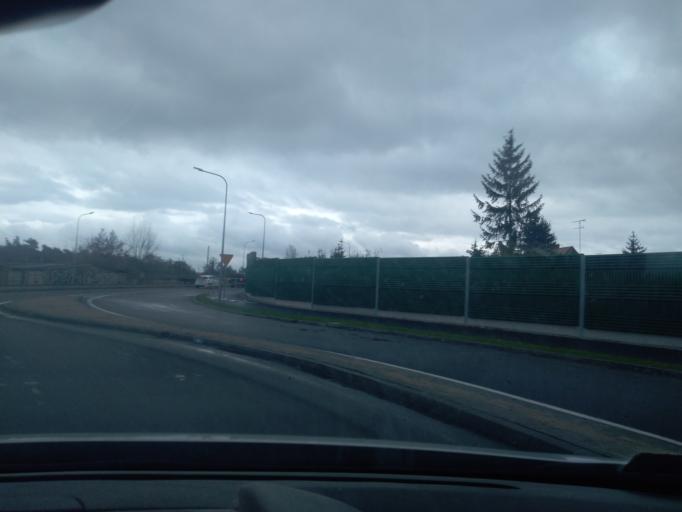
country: PL
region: Greater Poland Voivodeship
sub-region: Powiat obornicki
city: Oborniki
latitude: 52.6544
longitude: 16.8222
